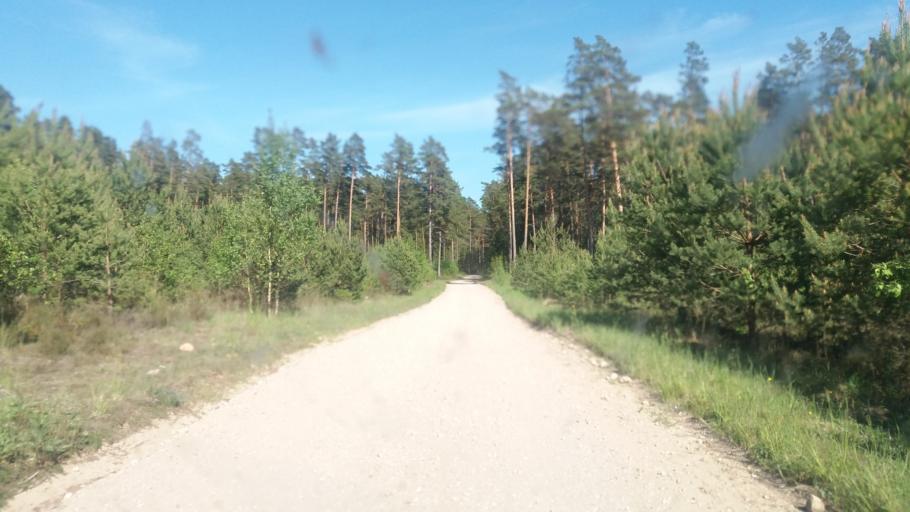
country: LV
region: Ventspils Rajons
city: Piltene
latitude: 57.0800
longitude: 21.7962
